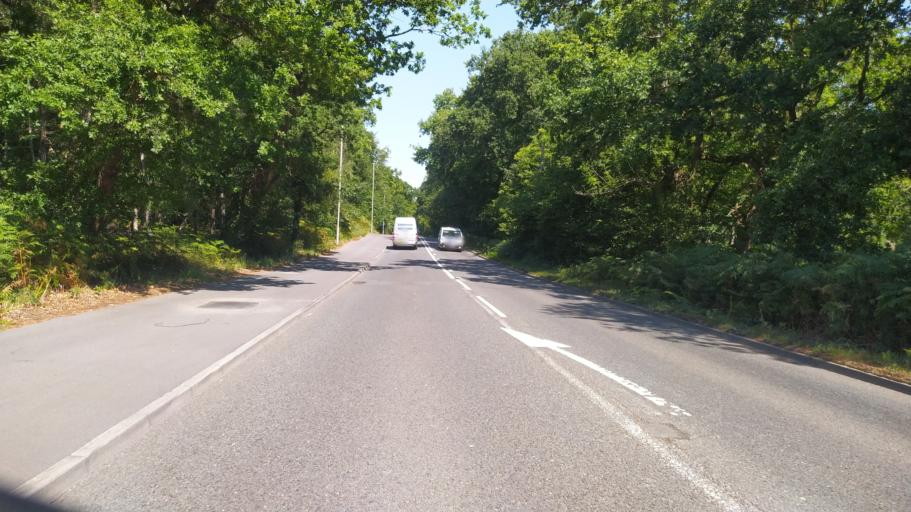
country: GB
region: England
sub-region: Dorset
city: Wimborne Minster
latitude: 50.7688
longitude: -1.9786
